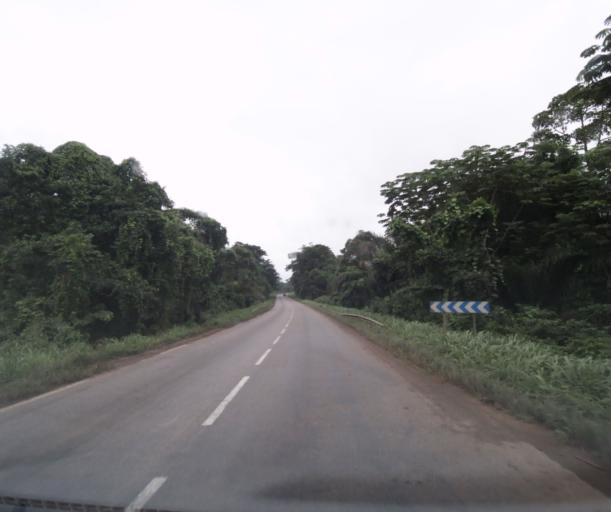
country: CM
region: Centre
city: Eseka
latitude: 3.8490
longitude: 10.4840
